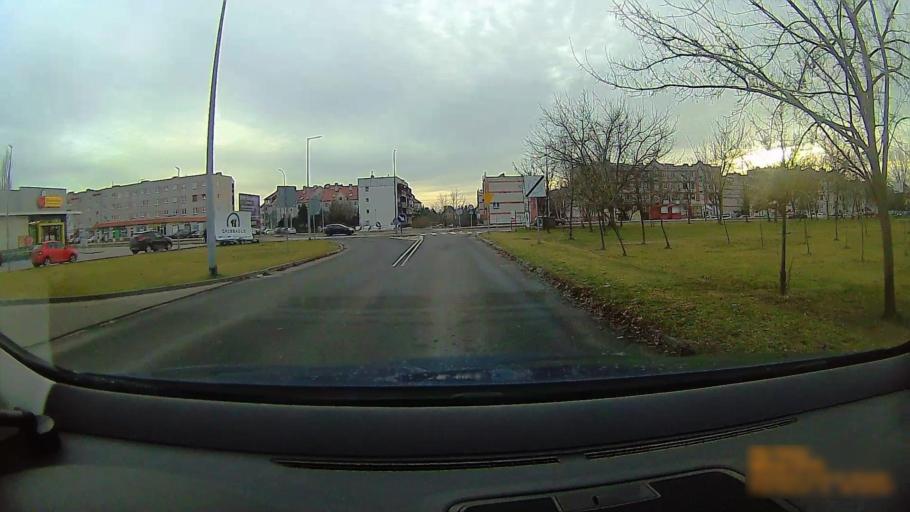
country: PL
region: Greater Poland Voivodeship
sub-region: Konin
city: Konin
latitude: 52.2347
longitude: 18.2203
